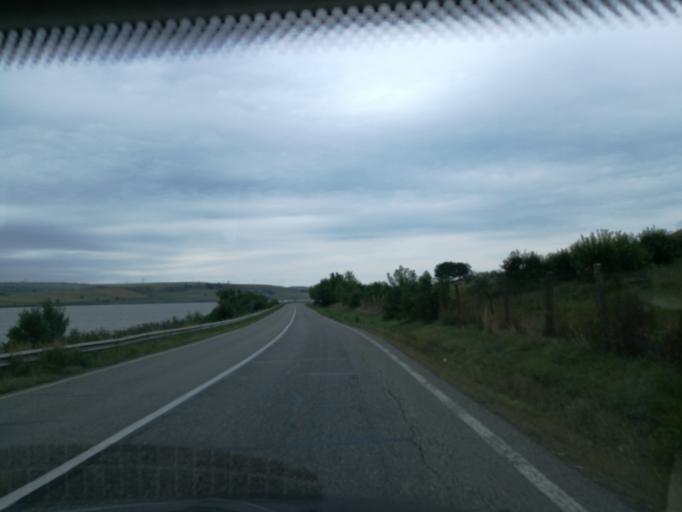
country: RO
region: Suceava
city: Bunesti-Regat
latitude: 47.4889
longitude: 26.2904
